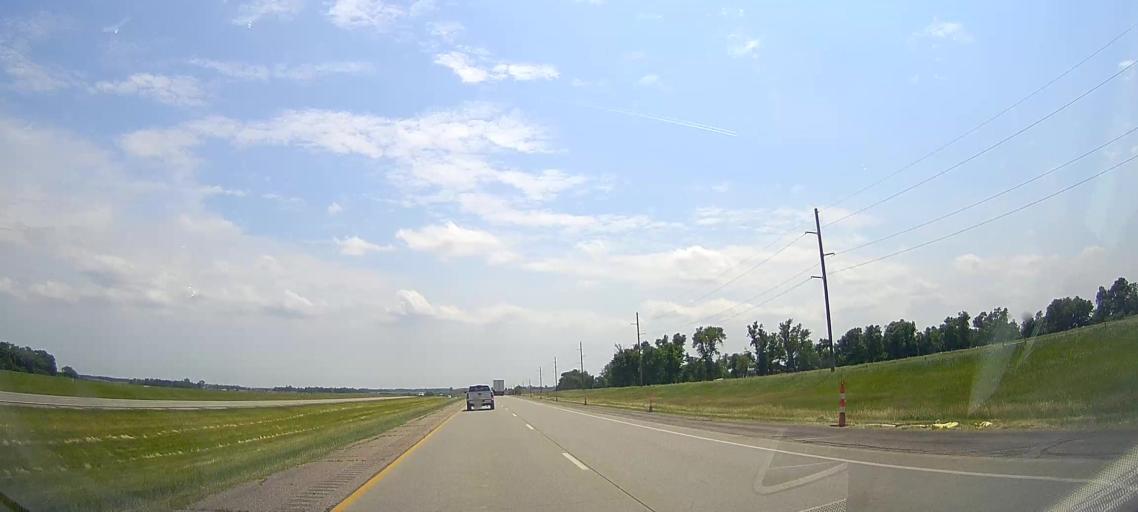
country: US
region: South Dakota
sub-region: Lincoln County
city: Tea
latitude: 43.3771
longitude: -96.7964
